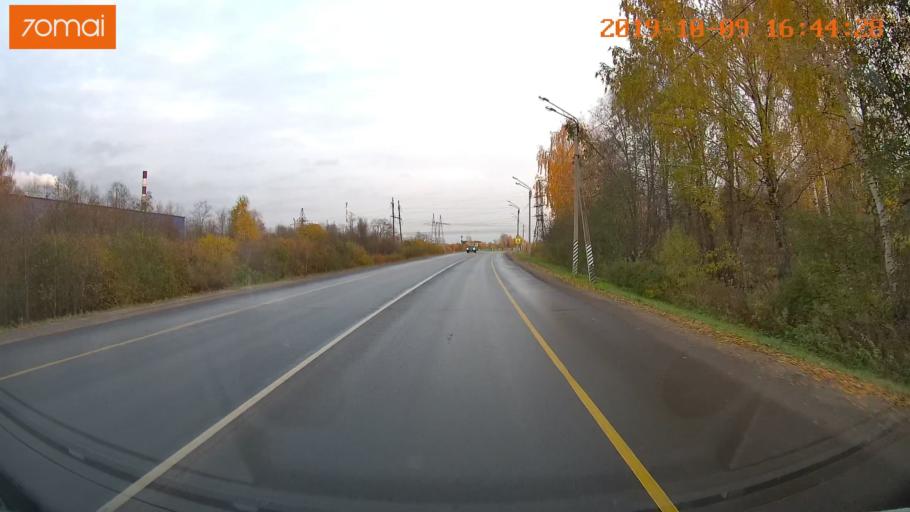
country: RU
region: Kostroma
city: Volgorechensk
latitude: 57.4516
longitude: 41.1412
